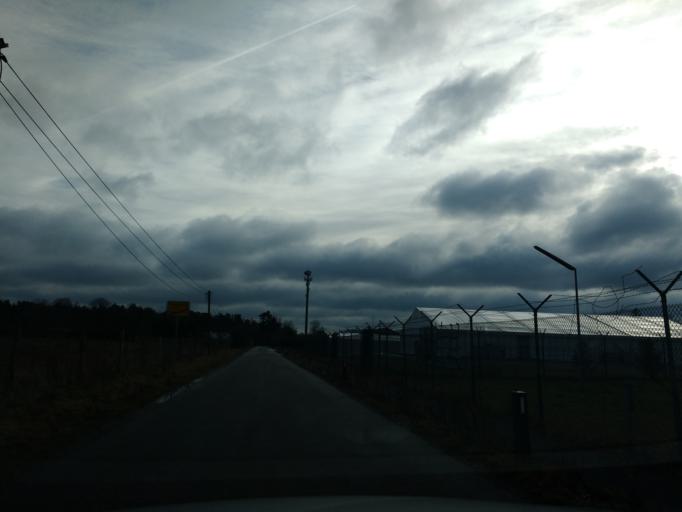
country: DE
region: North Rhine-Westphalia
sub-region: Regierungsbezirk Detmold
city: Hovelhof
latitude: 51.8672
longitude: 8.6790
